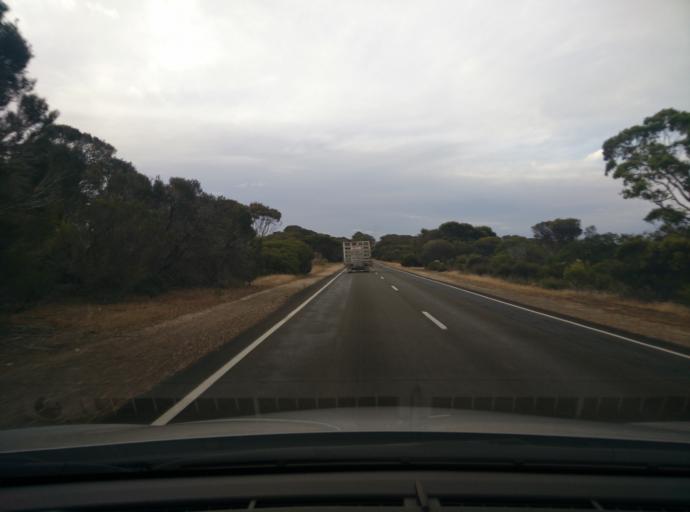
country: AU
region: South Australia
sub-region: Kangaroo Island
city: Kingscote
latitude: -35.7594
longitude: 137.6070
